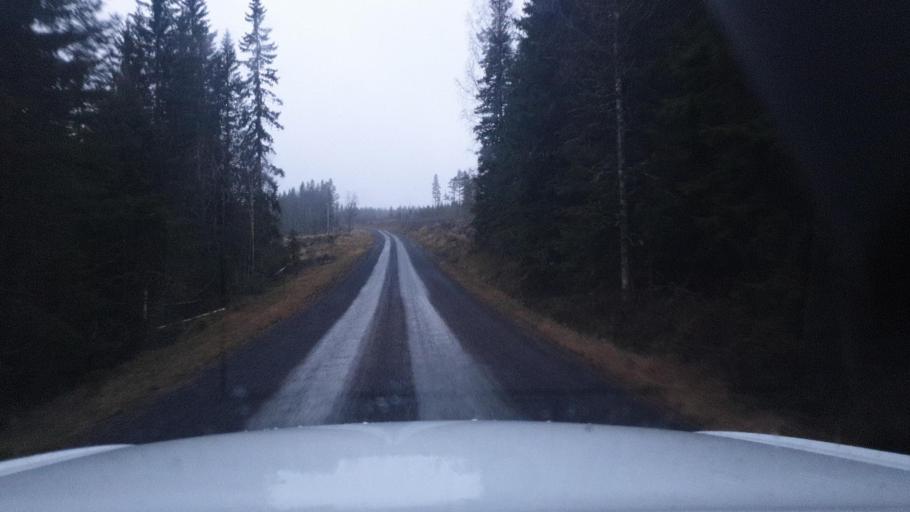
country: SE
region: Vaermland
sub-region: Torsby Kommun
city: Torsby
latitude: 60.1799
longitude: 12.6455
